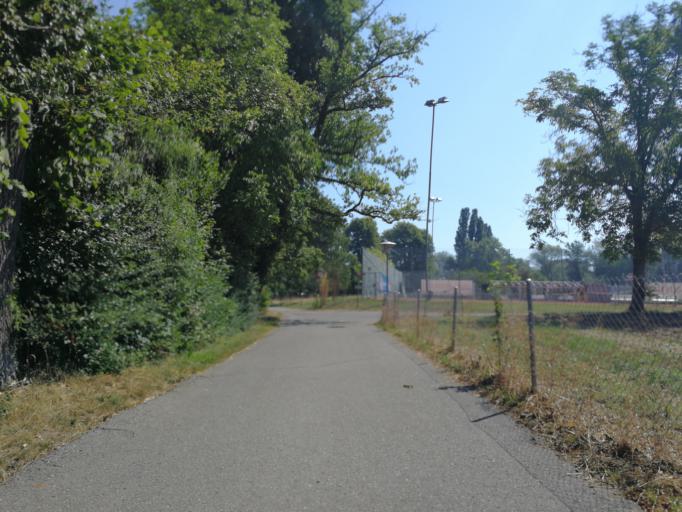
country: CH
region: Thurgau
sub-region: Kreuzlingen District
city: Munsterlingen
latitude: 47.6327
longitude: 9.2386
